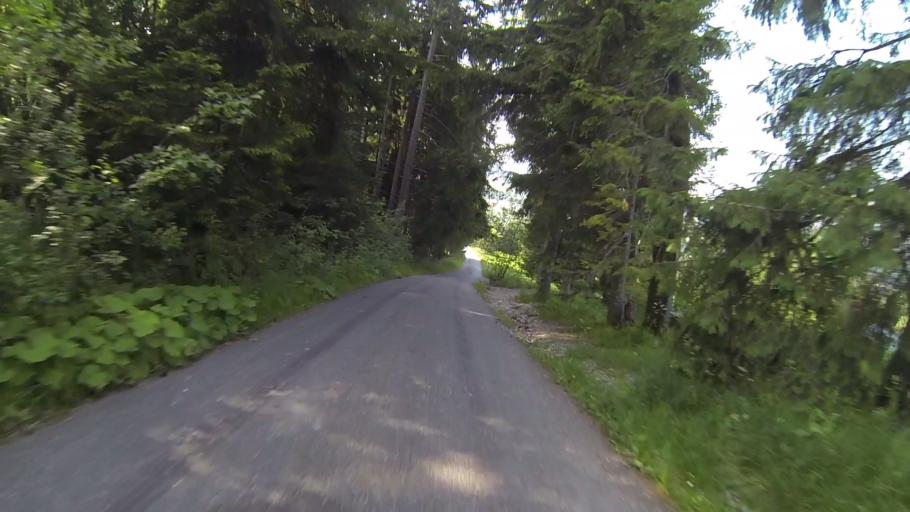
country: DE
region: Bavaria
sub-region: Swabia
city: Nesselwang
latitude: 47.6090
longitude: 10.4988
